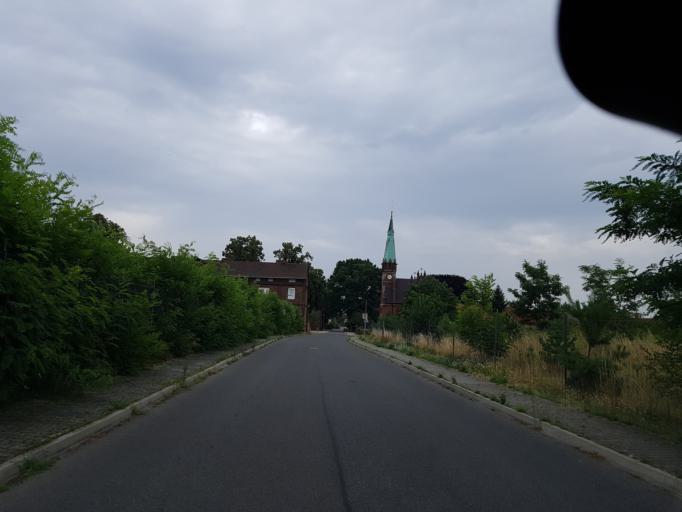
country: DE
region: Brandenburg
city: Schipkau
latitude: 51.5627
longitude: 13.8893
